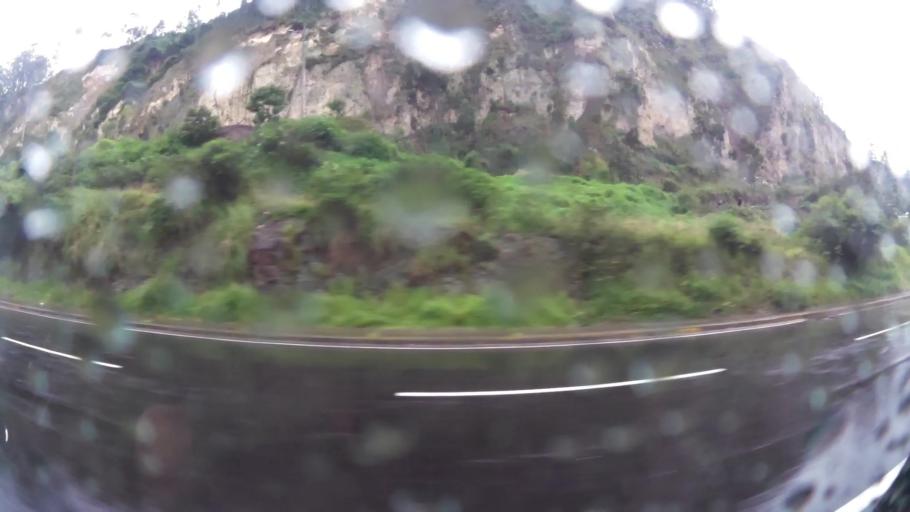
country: EC
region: Pichincha
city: Quito
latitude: -0.1520
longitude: -78.4593
